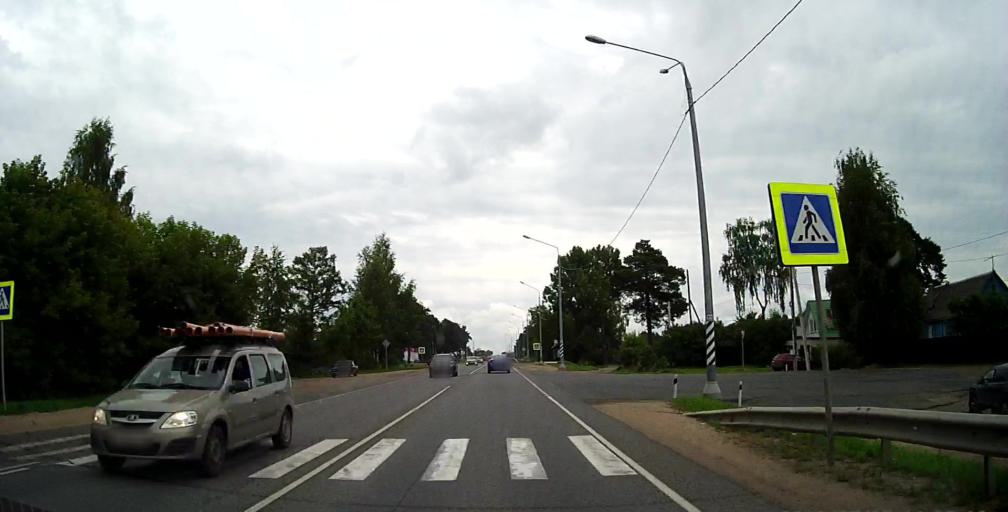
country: RU
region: Smolensk
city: Katyn'
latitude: 54.7839
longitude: 31.8389
